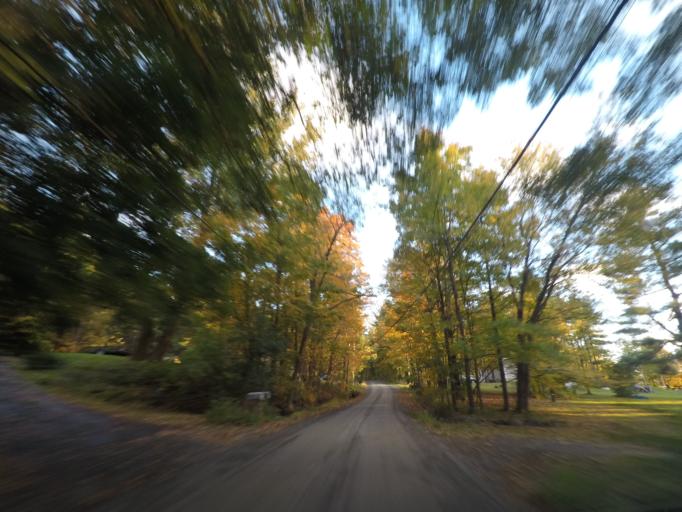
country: US
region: New York
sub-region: Rensselaer County
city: Nassau
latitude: 42.5136
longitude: -73.5910
